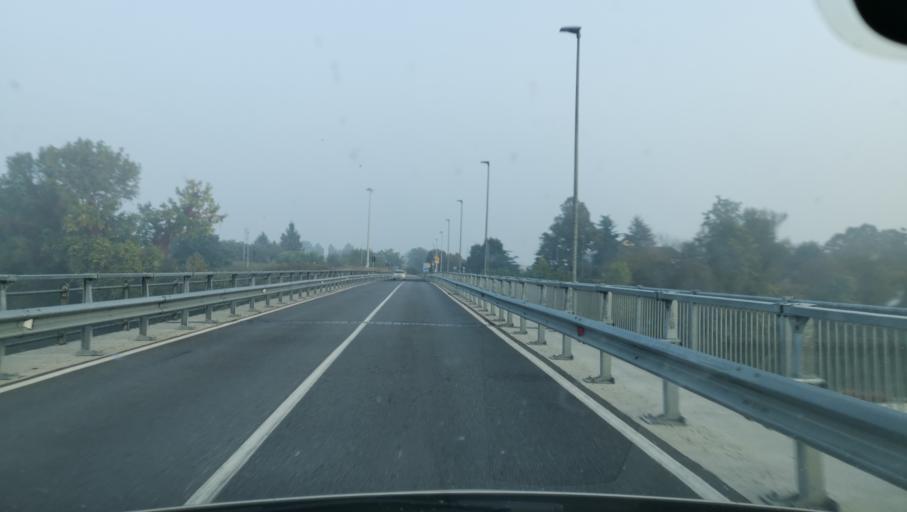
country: IT
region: Piedmont
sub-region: Provincia di Torino
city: Settimo Torinese
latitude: 45.1298
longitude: 7.7846
